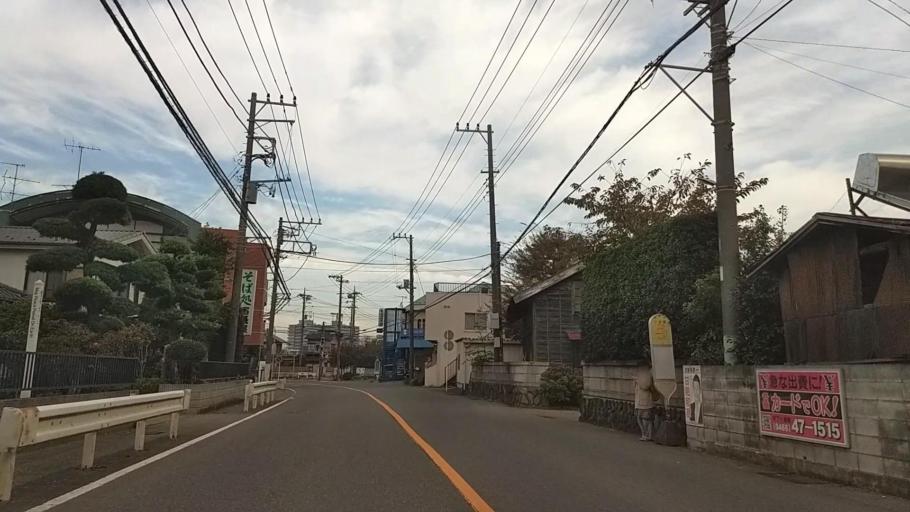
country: JP
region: Kanagawa
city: Fujisawa
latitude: 35.3970
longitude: 139.4404
